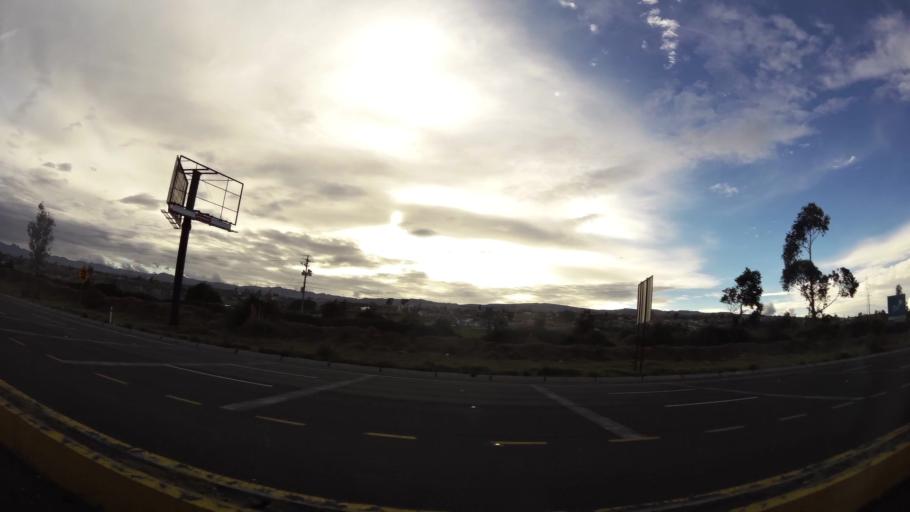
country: EC
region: Cotopaxi
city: Latacunga
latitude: -0.9063
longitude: -78.6284
